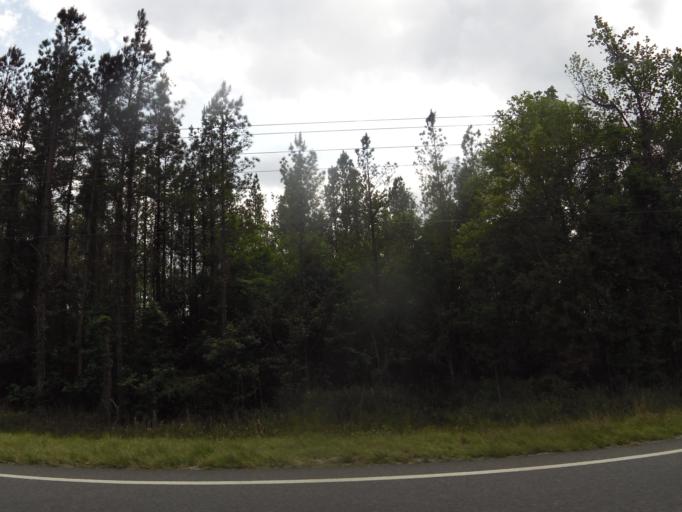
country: US
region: Florida
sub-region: Nassau County
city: Hilliard
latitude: 30.8182
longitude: -81.8504
